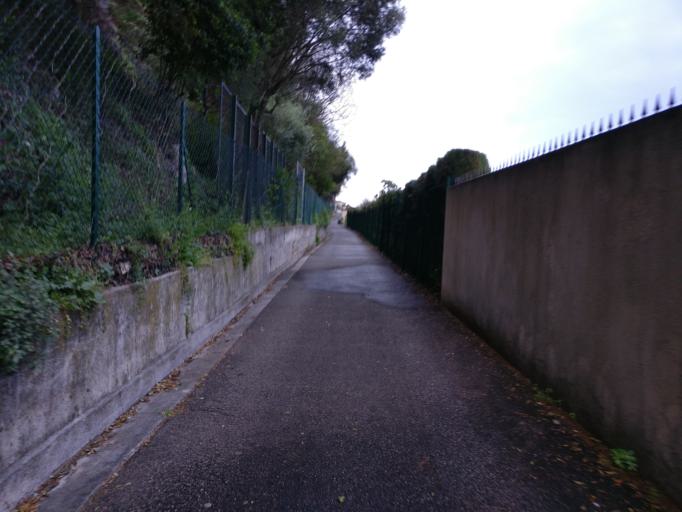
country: FR
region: Provence-Alpes-Cote d'Azur
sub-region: Departement des Alpes-Maritimes
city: Villefranche-sur-Mer
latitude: 43.7157
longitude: 7.2973
